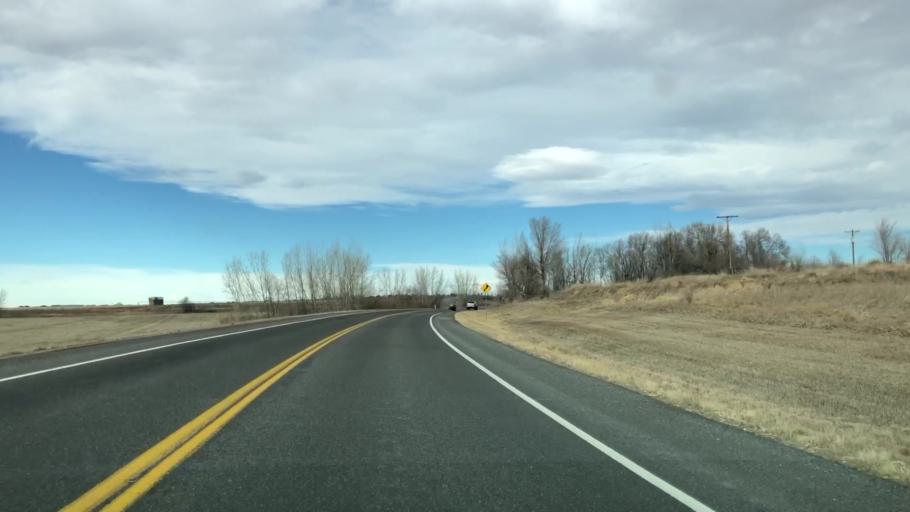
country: US
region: Colorado
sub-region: Weld County
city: Windsor
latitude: 40.5110
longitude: -104.9272
